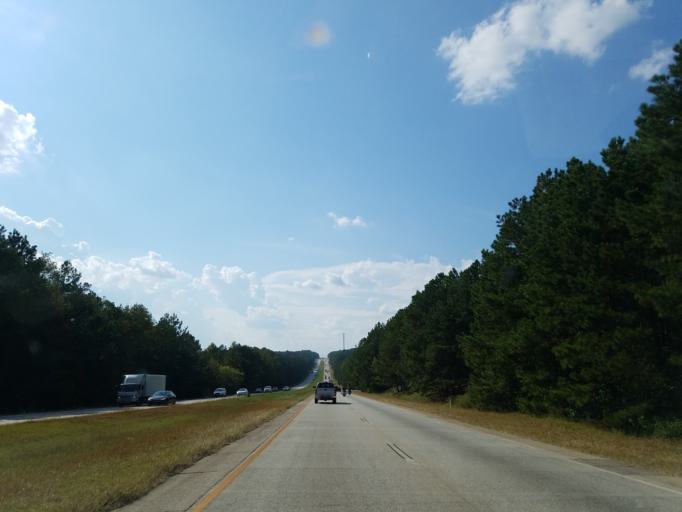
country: US
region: Georgia
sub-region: Barrow County
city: Winder
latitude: 33.9568
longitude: -83.7797
